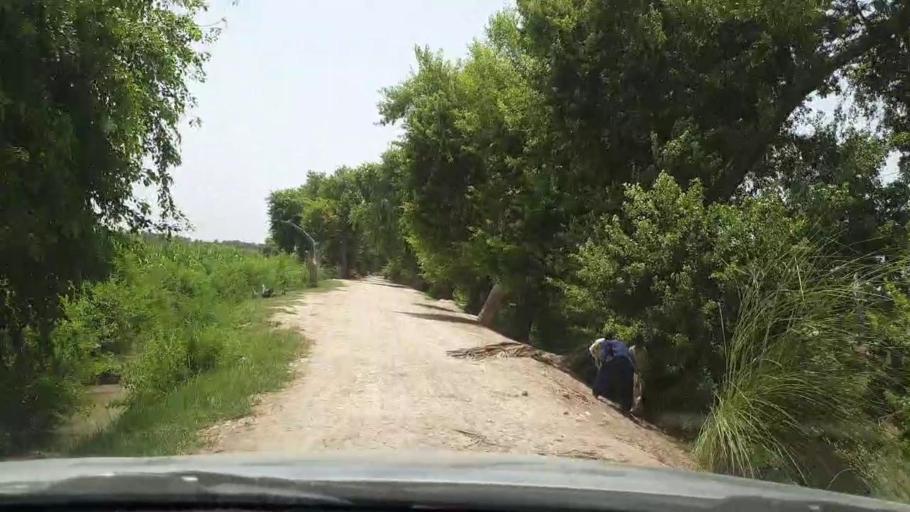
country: PK
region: Sindh
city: Pano Aqil
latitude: 27.8572
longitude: 69.0879
